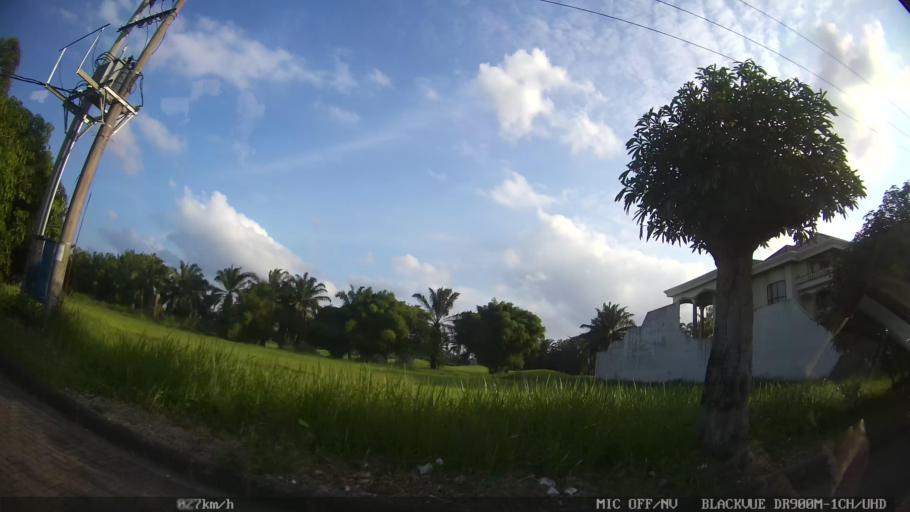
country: ID
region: North Sumatra
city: Medan
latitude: 3.6243
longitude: 98.6562
